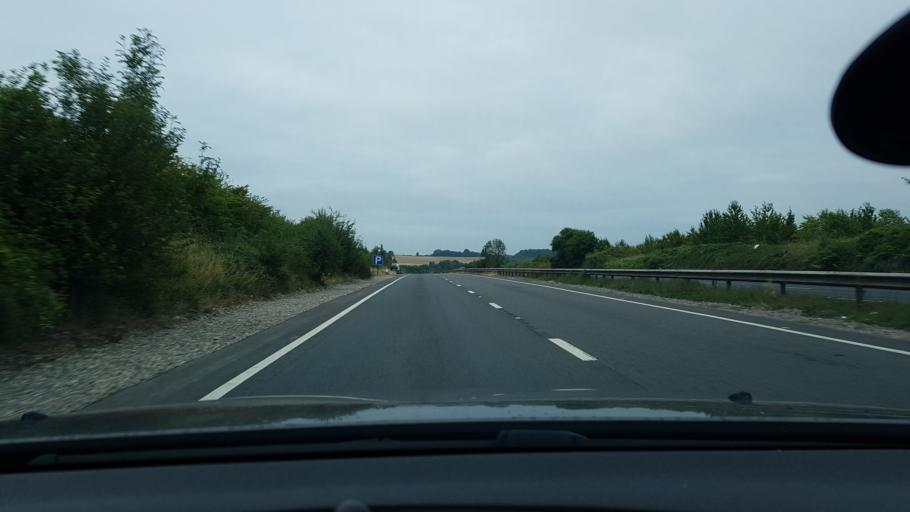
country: GB
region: England
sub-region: Hampshire
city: Overton
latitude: 51.2075
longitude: -1.3395
